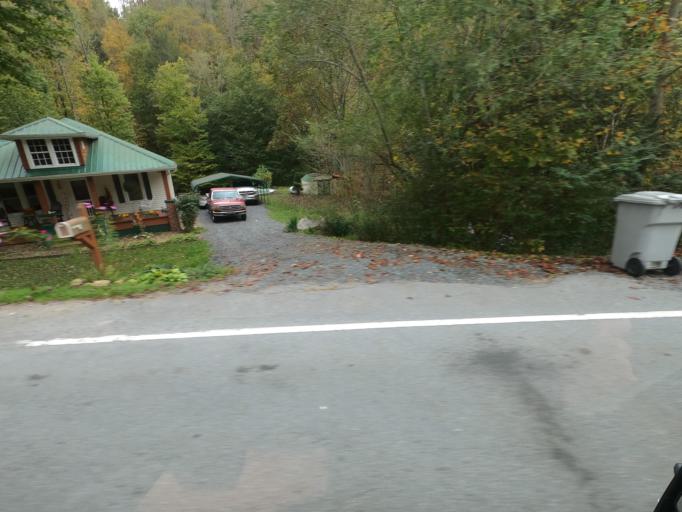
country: US
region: Tennessee
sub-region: Carter County
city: Roan Mountain
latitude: 36.2220
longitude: -82.1784
